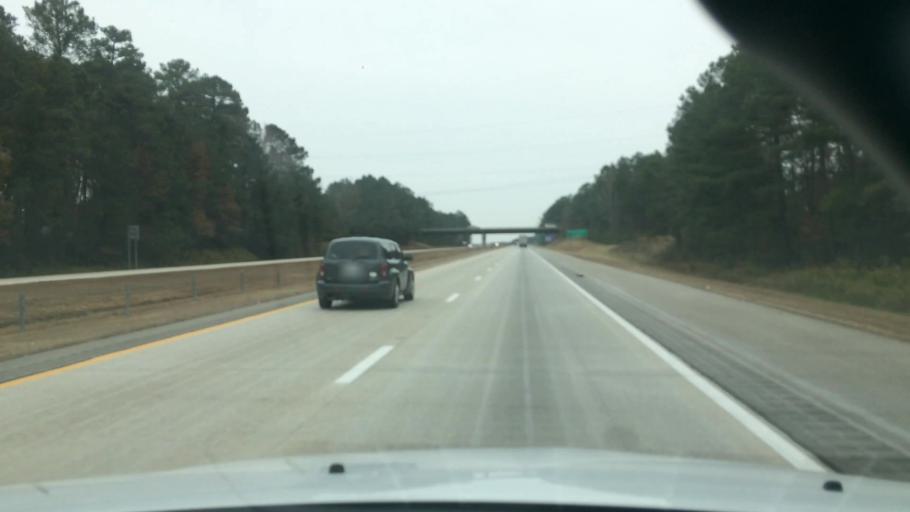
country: US
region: North Carolina
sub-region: Nash County
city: Red Oak
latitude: 35.9662
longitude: -77.8831
